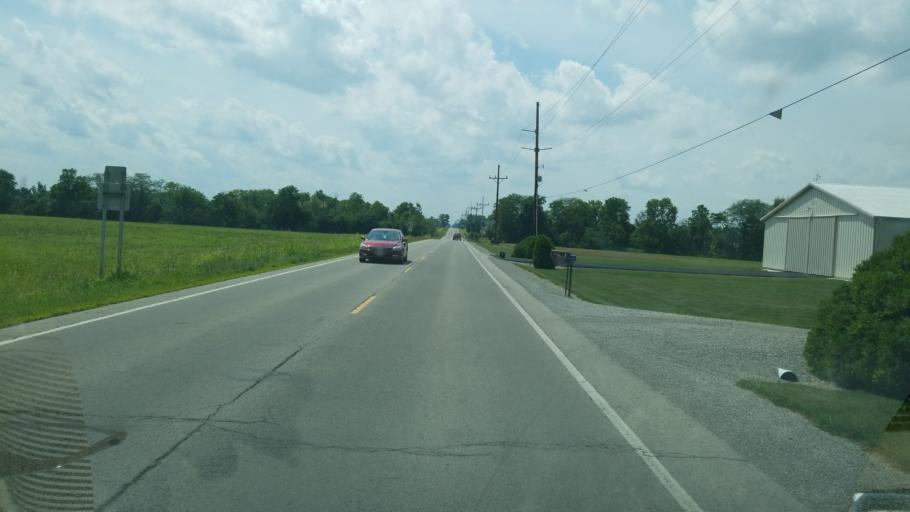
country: US
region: Ohio
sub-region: Hancock County
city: Findlay
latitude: 40.9844
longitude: -83.7289
